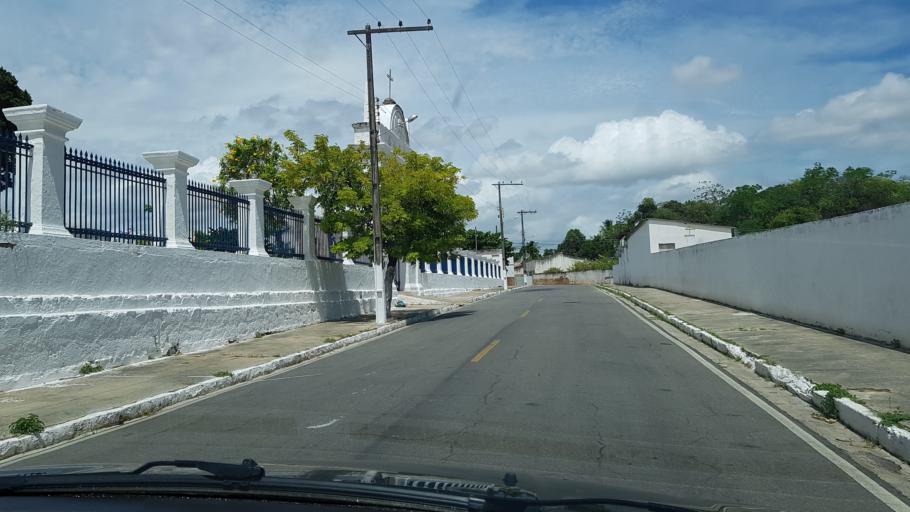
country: BR
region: Alagoas
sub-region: Penedo
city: Penedo
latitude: -10.2832
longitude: -36.5737
